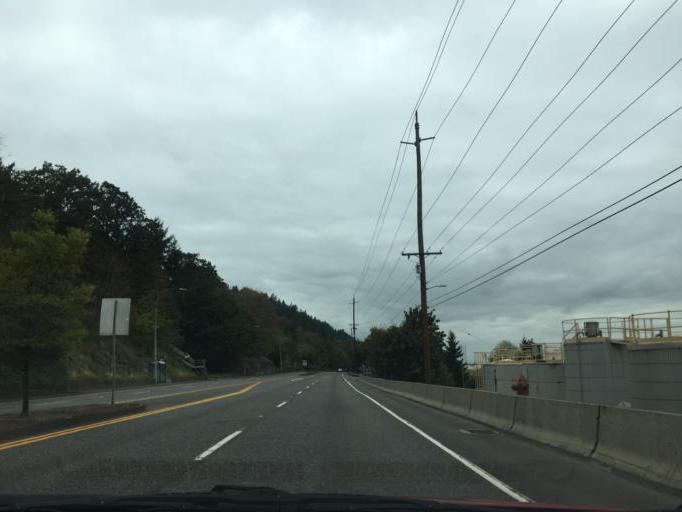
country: US
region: Oregon
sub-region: Washington County
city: Cedar Mill
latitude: 45.5917
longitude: -122.7799
